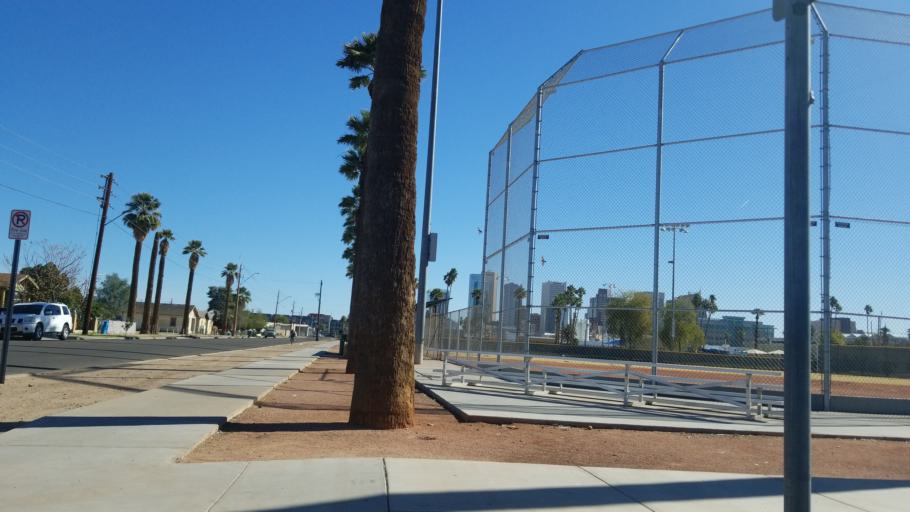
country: US
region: Arizona
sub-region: Maricopa County
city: Phoenix
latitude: 33.4531
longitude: -112.0884
